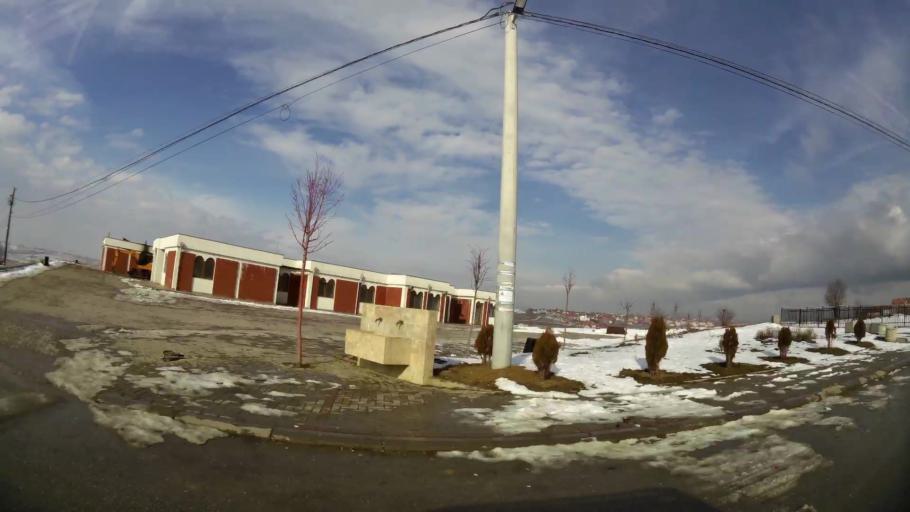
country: XK
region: Pristina
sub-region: Komuna e Prishtines
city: Pristina
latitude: 42.6744
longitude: 21.1496
